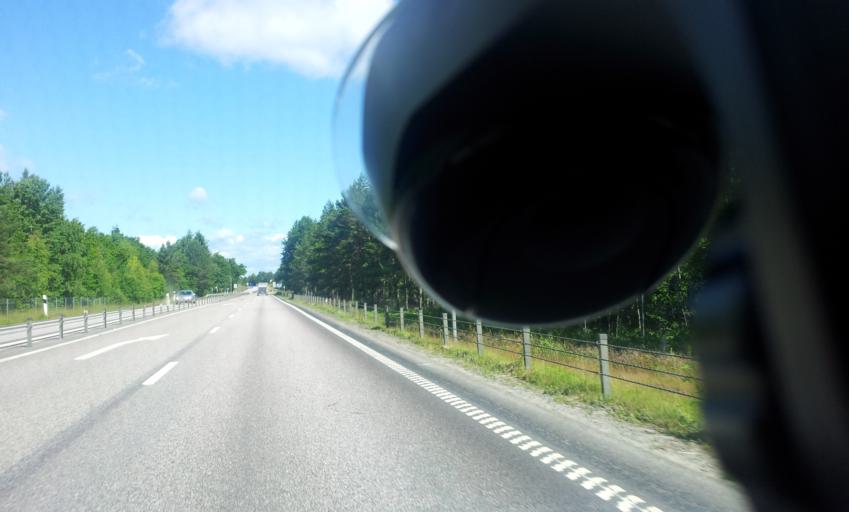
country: SE
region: Kalmar
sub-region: Oskarshamns Kommun
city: Paskallavik
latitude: 57.1379
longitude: 16.4715
